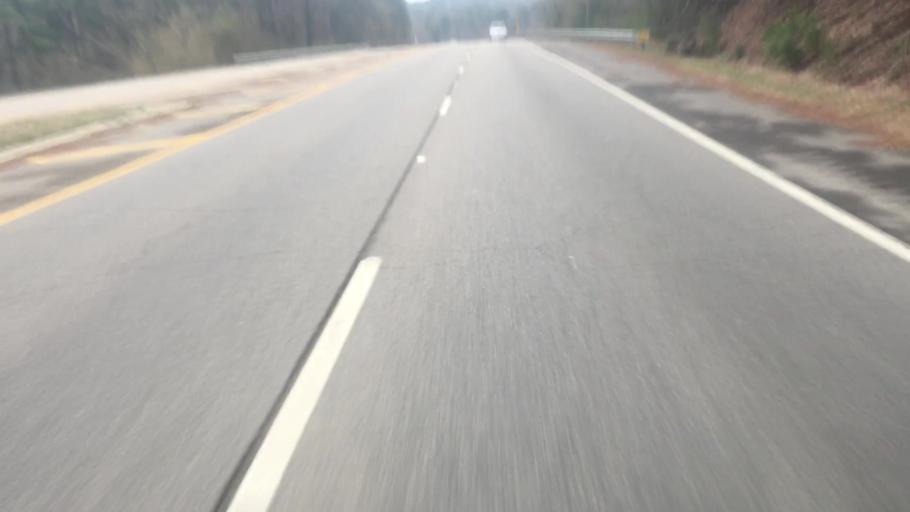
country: US
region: Alabama
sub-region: Walker County
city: Sumiton
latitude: 33.7526
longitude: -87.0602
